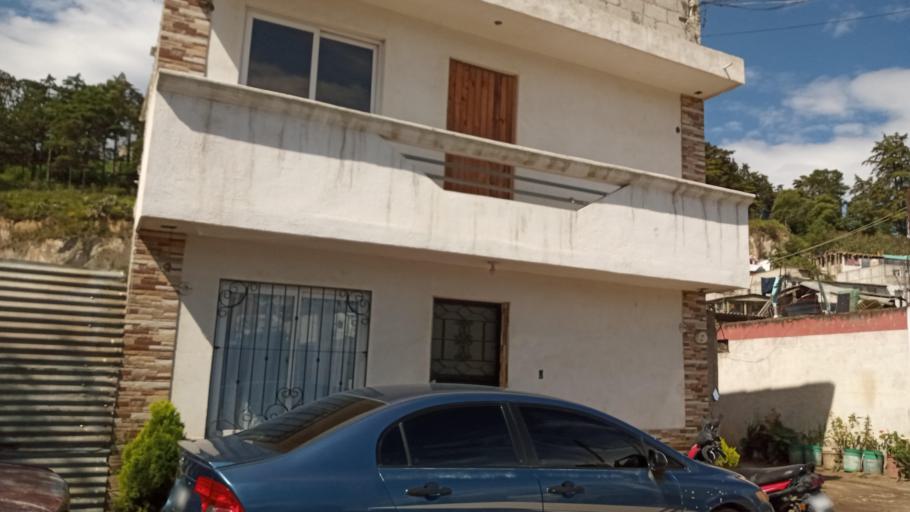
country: GT
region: Quetzaltenango
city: Quetzaltenango
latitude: 14.8471
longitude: -91.5109
